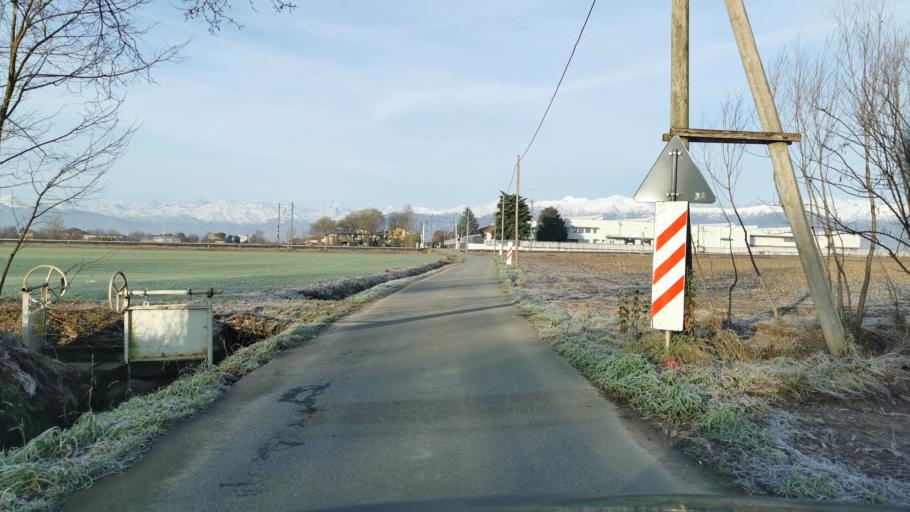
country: IT
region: Piedmont
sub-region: Provincia di Torino
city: Feletto
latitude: 45.2870
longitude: 7.7543
